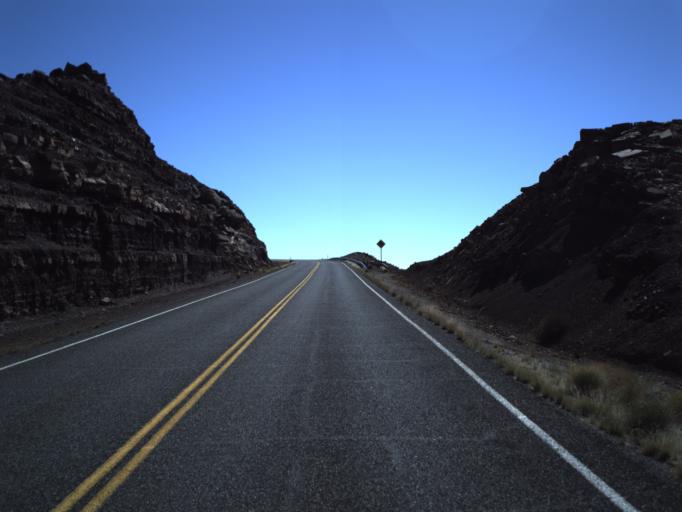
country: US
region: Utah
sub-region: San Juan County
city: Blanding
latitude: 37.8834
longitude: -110.4252
